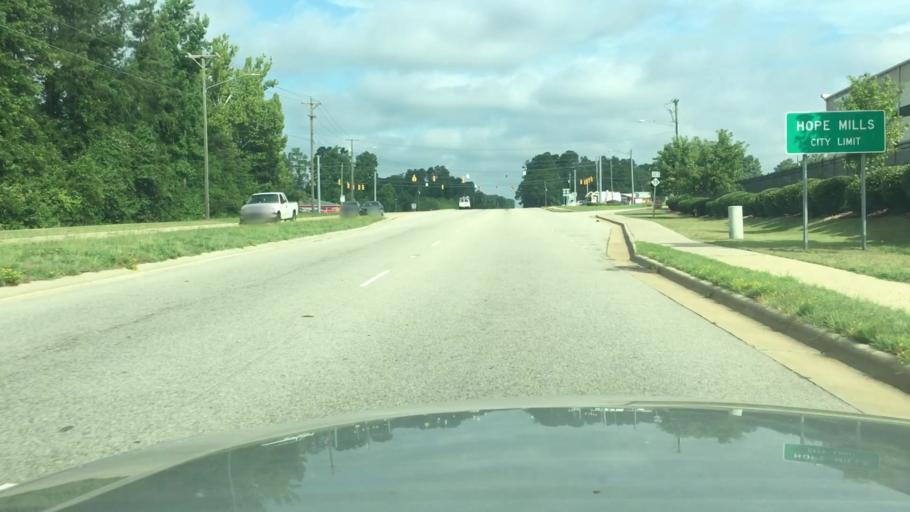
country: US
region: North Carolina
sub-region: Cumberland County
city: Hope Mills
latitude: 34.9944
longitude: -78.9659
